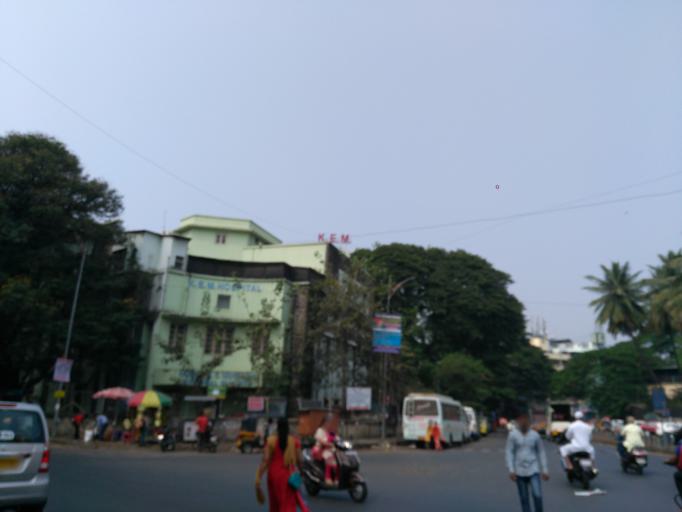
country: IN
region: Maharashtra
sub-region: Pune Division
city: Pune
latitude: 18.5196
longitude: 73.8681
